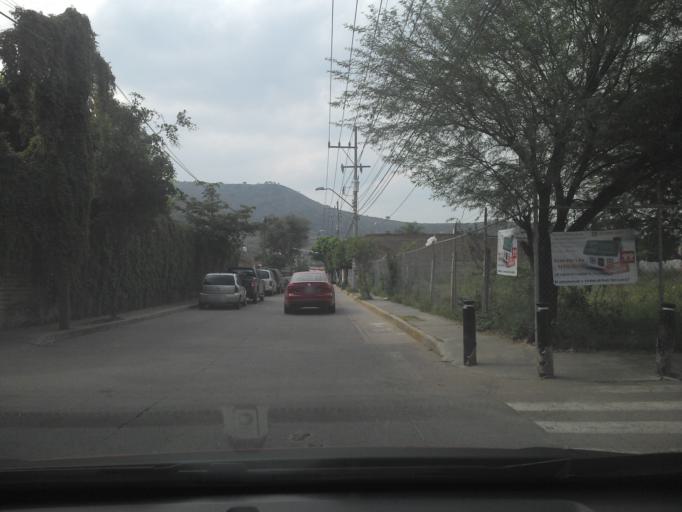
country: MX
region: Jalisco
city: Tlajomulco de Zuniga
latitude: 20.4780
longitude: -103.4506
